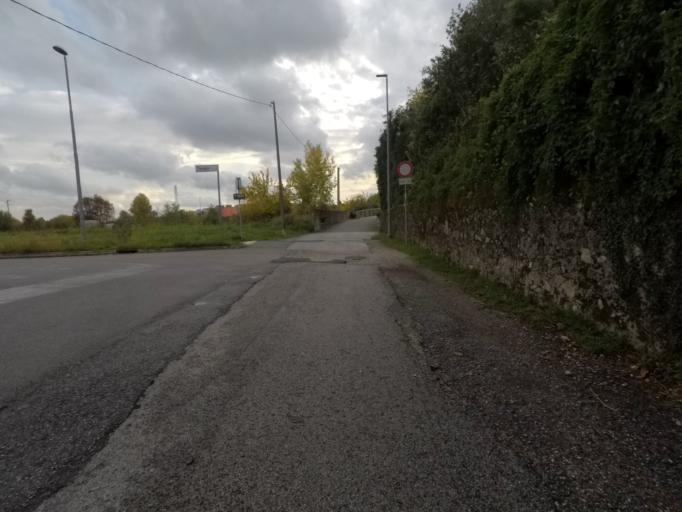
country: IT
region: Friuli Venezia Giulia
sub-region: Provincia di Udine
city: Colugna
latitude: 46.0825
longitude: 13.2050
